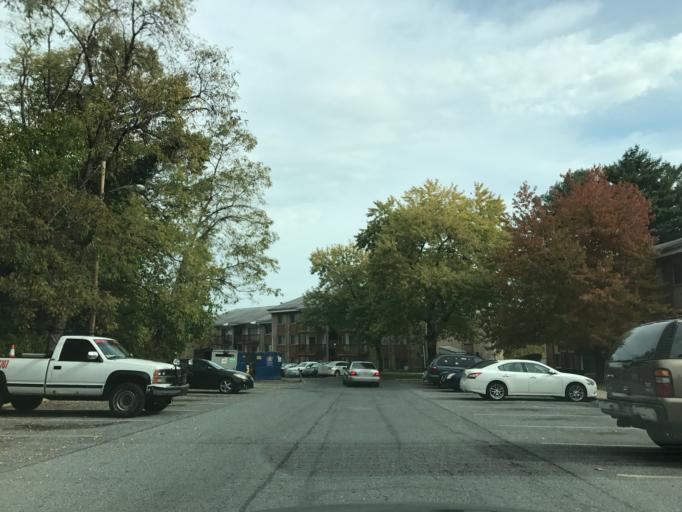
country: US
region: Maryland
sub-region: Baltimore County
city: Lochearn
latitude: 39.3418
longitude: -76.6595
